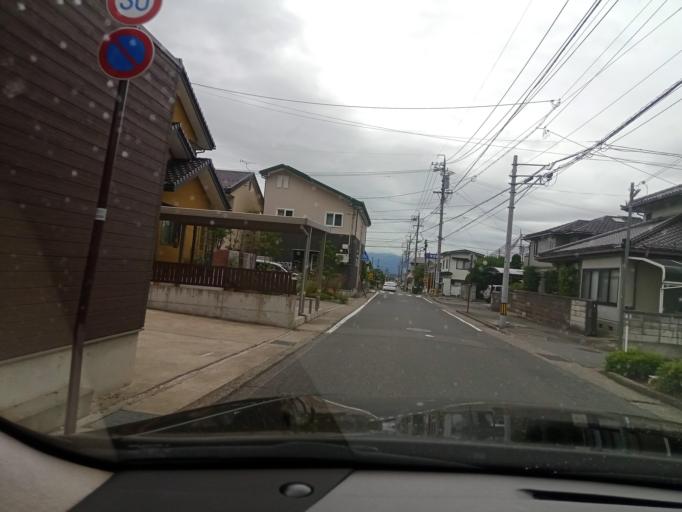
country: JP
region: Nagano
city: Nagano-shi
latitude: 36.6821
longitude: 138.2079
